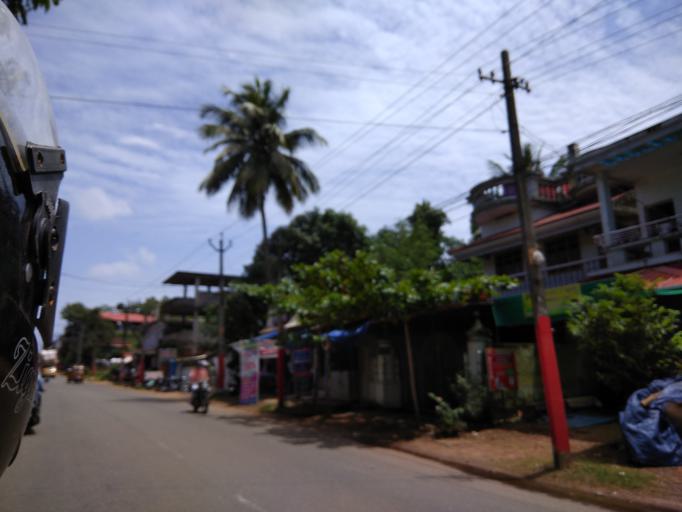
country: IN
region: Kerala
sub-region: Thrissur District
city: Trichur
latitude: 10.4979
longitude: 76.1611
